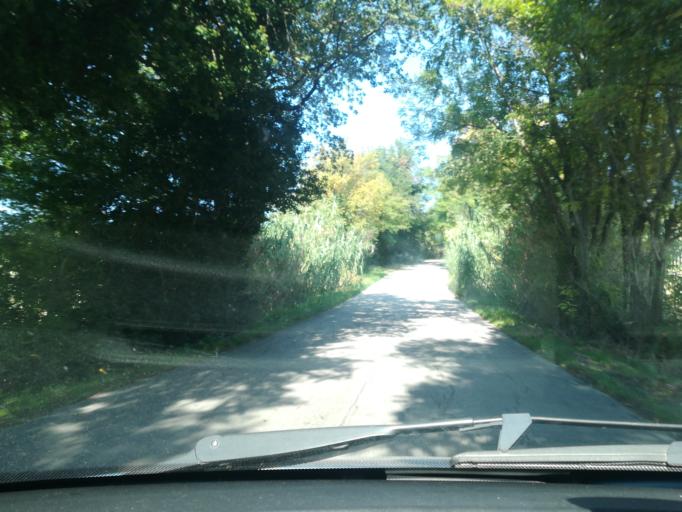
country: IT
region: The Marches
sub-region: Provincia di Macerata
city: Sforzacosta
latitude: 43.2658
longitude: 13.4530
